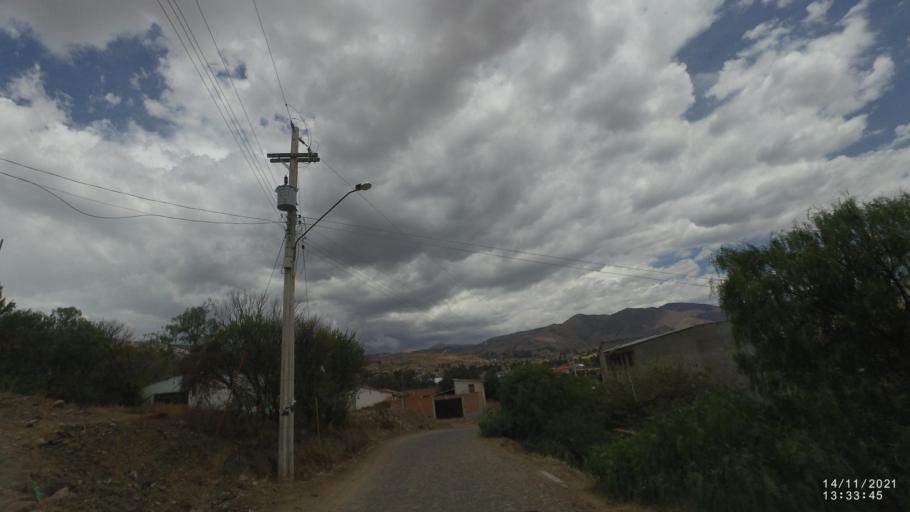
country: BO
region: Cochabamba
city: Colomi
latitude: -17.3995
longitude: -65.9846
